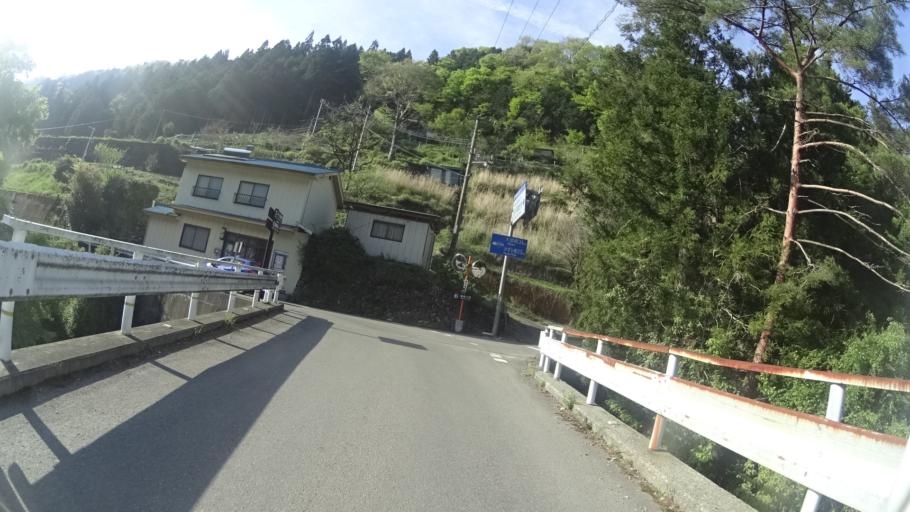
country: JP
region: Tokushima
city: Ikedacho
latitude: 33.8745
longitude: 133.9913
